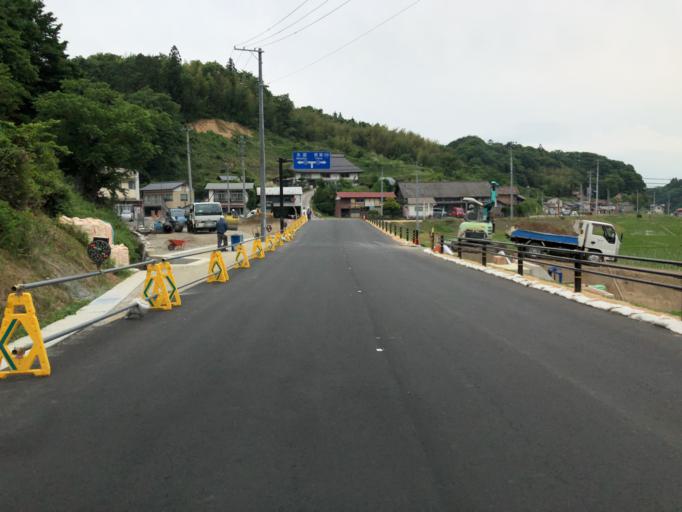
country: JP
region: Fukushima
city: Funehikimachi-funehiki
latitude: 37.4846
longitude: 140.5444
